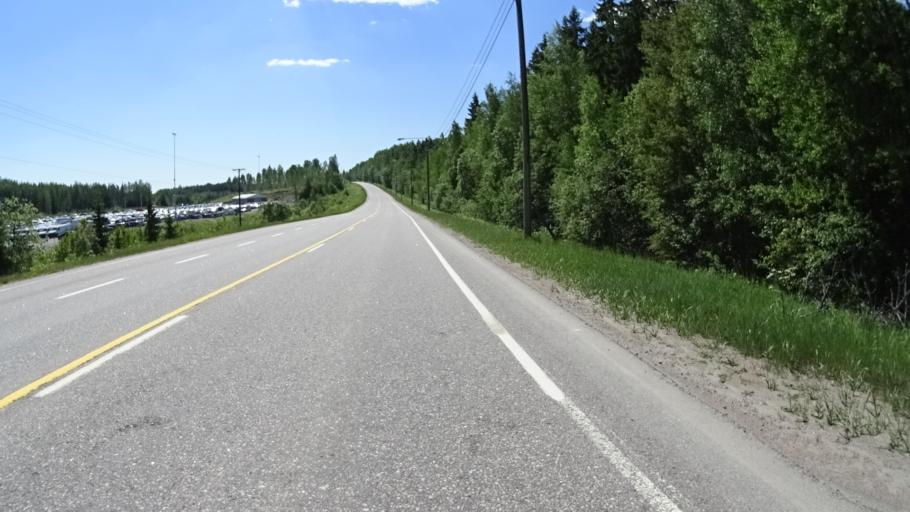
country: FI
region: Uusimaa
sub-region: Helsinki
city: Nurmijaervi
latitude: 60.3717
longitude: 24.8053
